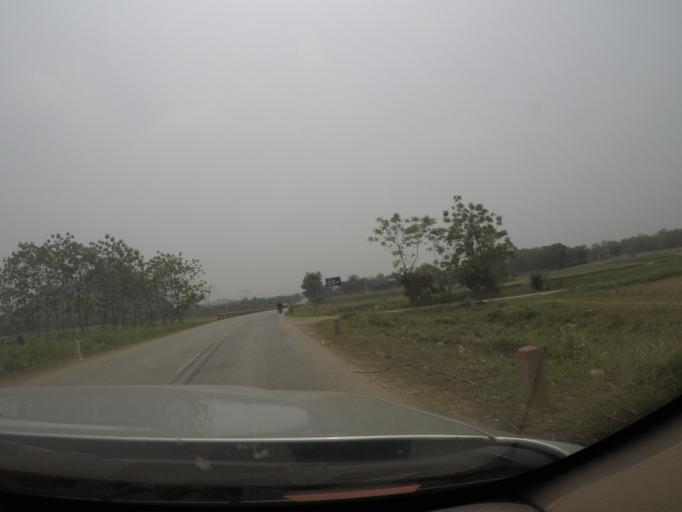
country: VN
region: Thanh Hoa
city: Thi Tran Thuong Xuan
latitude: 19.9228
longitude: 105.3946
